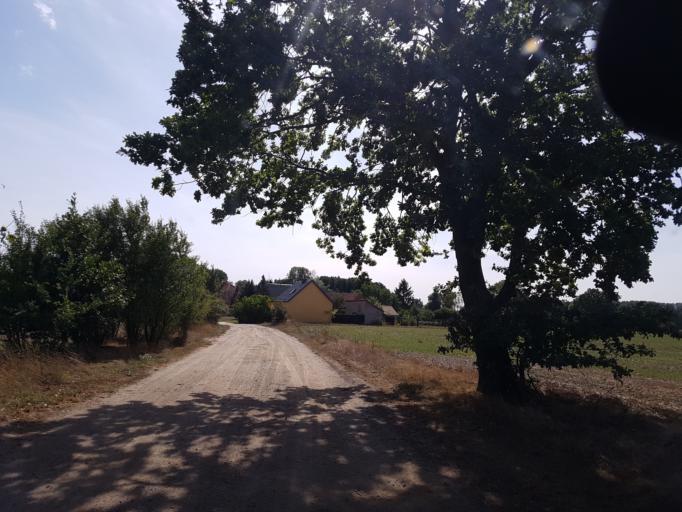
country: DE
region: Brandenburg
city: Luckau
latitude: 51.8669
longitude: 13.6460
